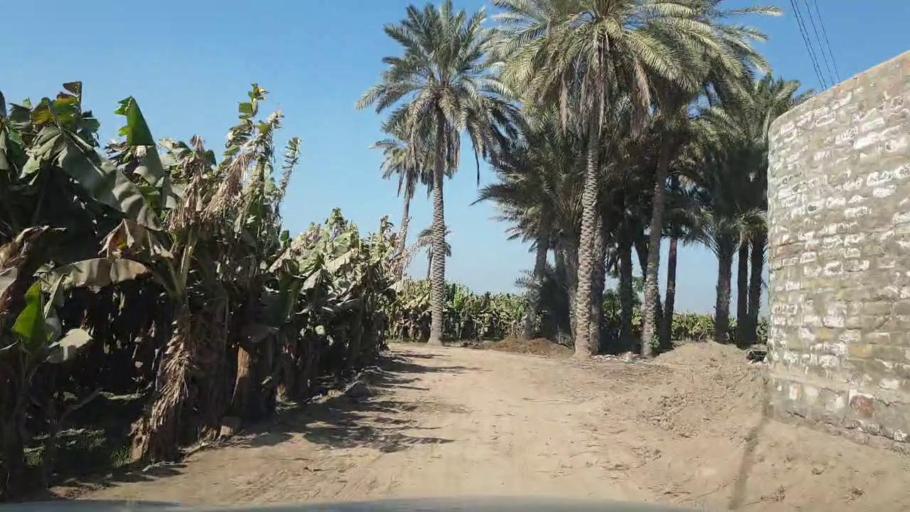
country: PK
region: Sindh
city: Tando Adam
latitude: 25.6377
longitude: 68.6731
